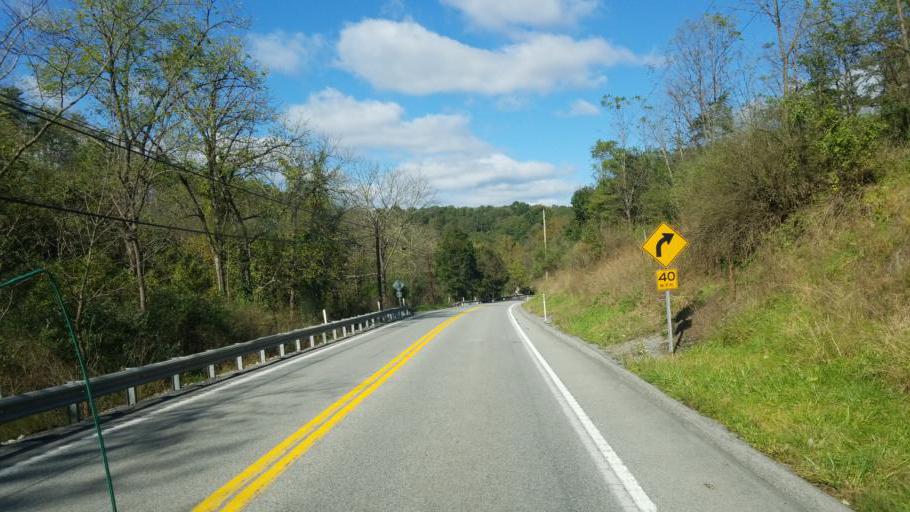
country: US
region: Pennsylvania
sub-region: Fulton County
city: McConnellsburg
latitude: 39.9776
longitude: -78.0416
